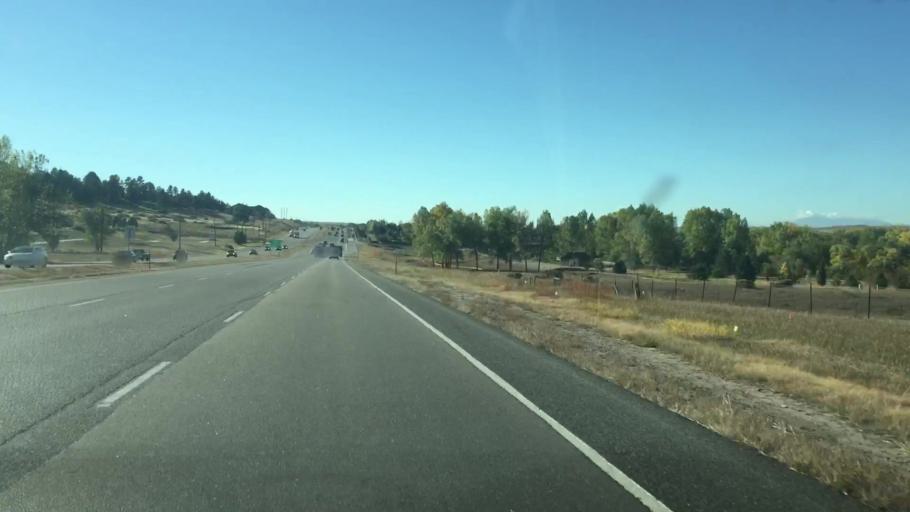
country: US
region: Colorado
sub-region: Douglas County
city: Parker
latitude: 39.5045
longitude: -104.7628
